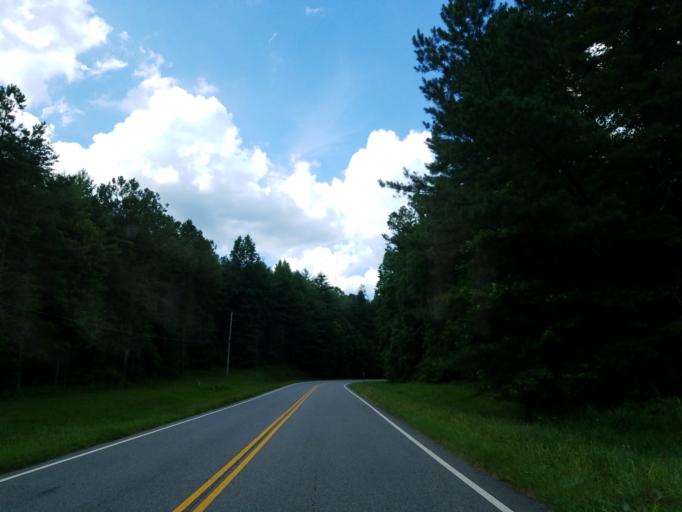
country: US
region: Georgia
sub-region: Lumpkin County
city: Dahlonega
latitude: 34.5164
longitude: -84.0601
